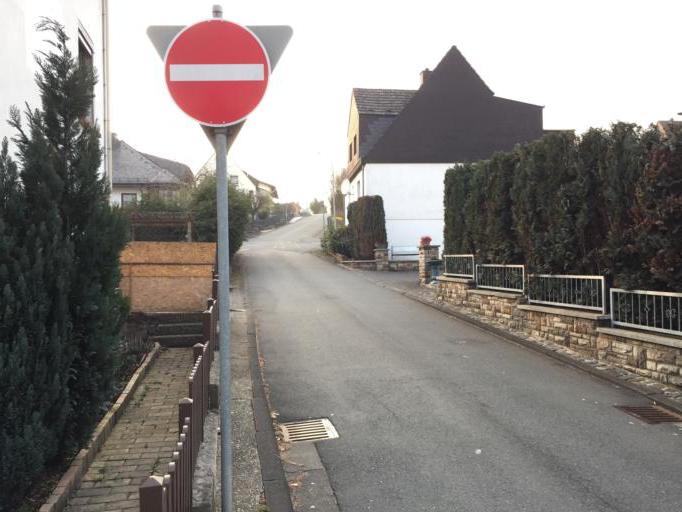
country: DE
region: Hesse
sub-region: Regierungsbezirk Giessen
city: Ehringshausen
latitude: 50.6041
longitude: 8.3823
